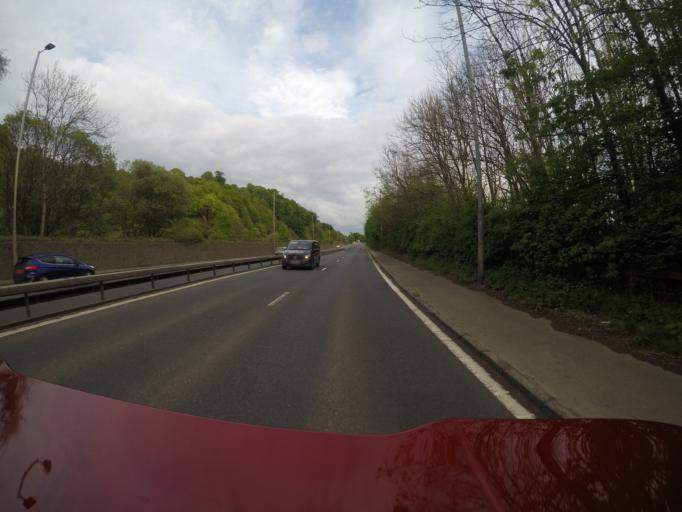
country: GB
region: Scotland
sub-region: Renfrewshire
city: Bishopton
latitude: 55.9342
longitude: -4.5112
